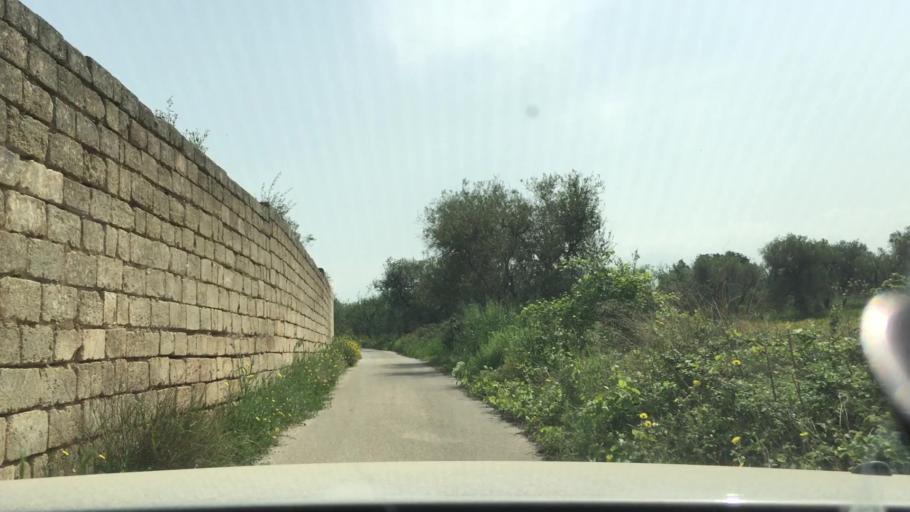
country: IT
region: Apulia
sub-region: Provincia di Barletta - Andria - Trani
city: Capirro
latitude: 41.2570
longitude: 16.4533
